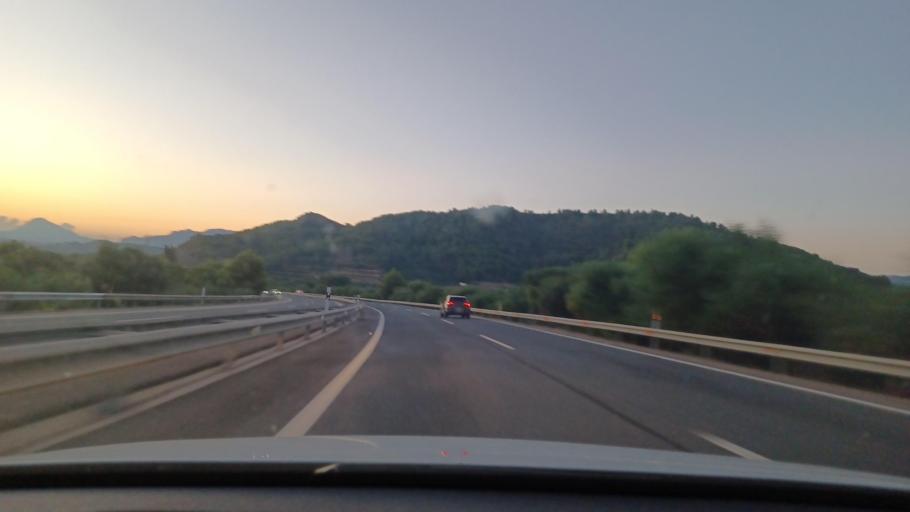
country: ES
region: Valencia
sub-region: Provincia de Valencia
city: Oliva
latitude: 38.9081
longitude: -0.1288
